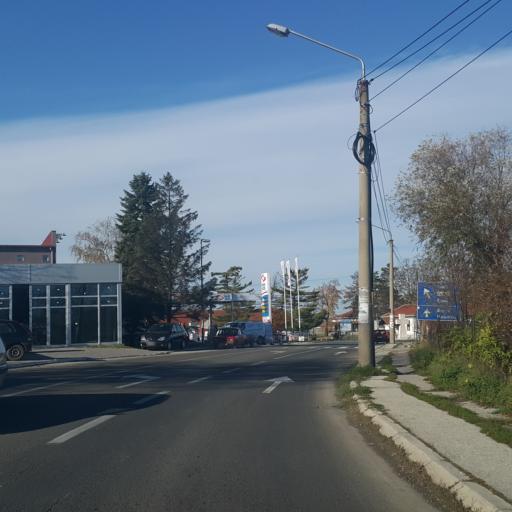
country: RS
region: Central Serbia
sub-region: Sumadijski Okrug
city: Topola
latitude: 44.2567
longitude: 20.6828
